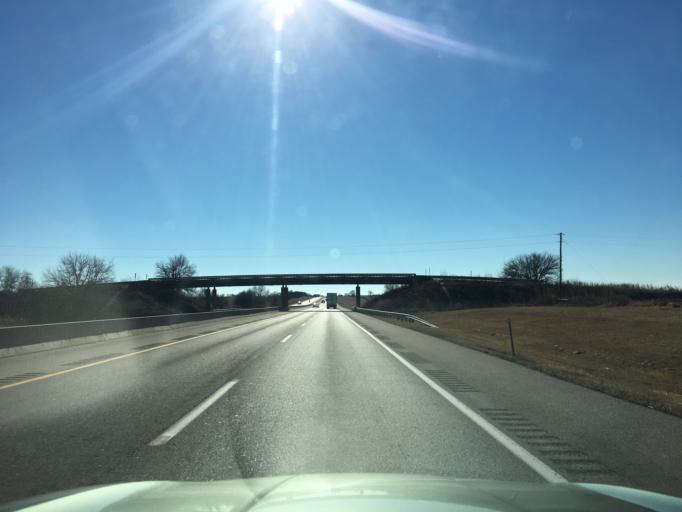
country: US
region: Kansas
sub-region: Sumner County
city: Wellington
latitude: 37.1169
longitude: -97.3389
